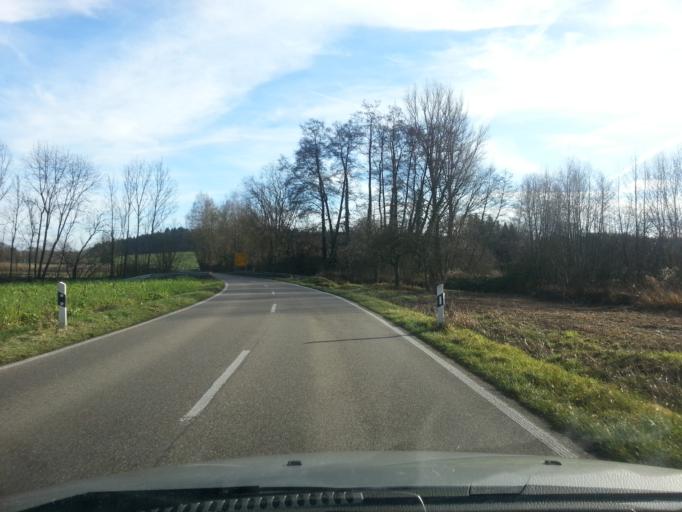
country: DE
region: Baden-Wuerttemberg
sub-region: Karlsruhe Region
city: Ostringen
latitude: 49.1727
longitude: 8.7597
